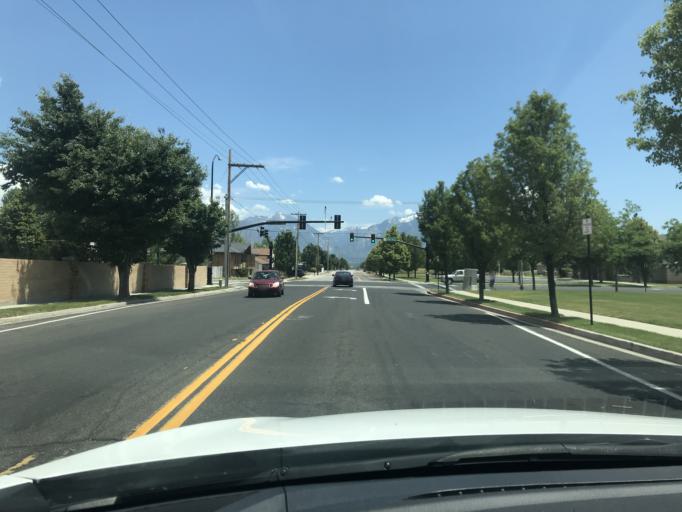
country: US
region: Utah
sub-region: Salt Lake County
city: South Jordan Heights
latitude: 40.5660
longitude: -111.9871
